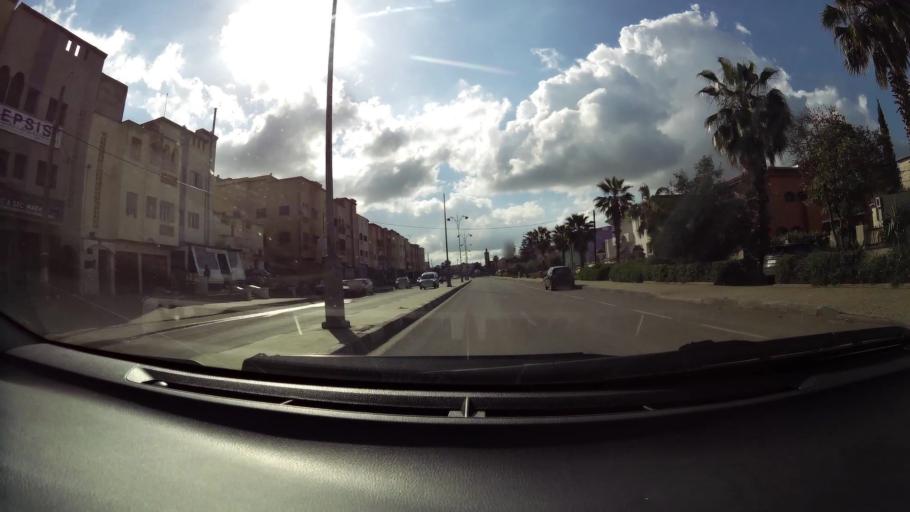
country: MA
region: Chaouia-Ouardigha
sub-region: Settat Province
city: Settat
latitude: 33.0085
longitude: -7.6271
